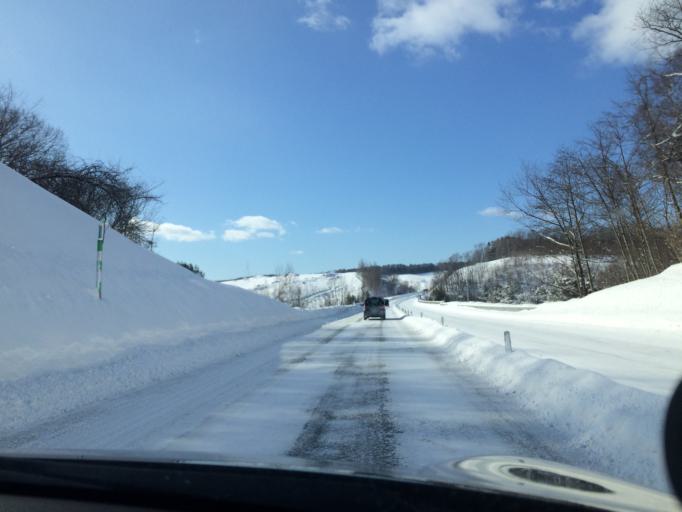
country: JP
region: Hokkaido
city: Chitose
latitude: 42.8830
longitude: 141.7585
